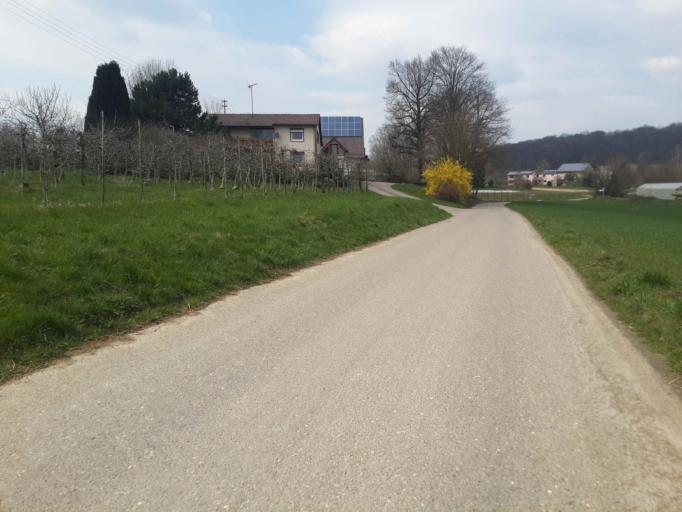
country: DE
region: Baden-Wuerttemberg
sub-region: Regierungsbezirk Stuttgart
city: Massenbachhausen
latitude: 49.1541
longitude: 9.0253
